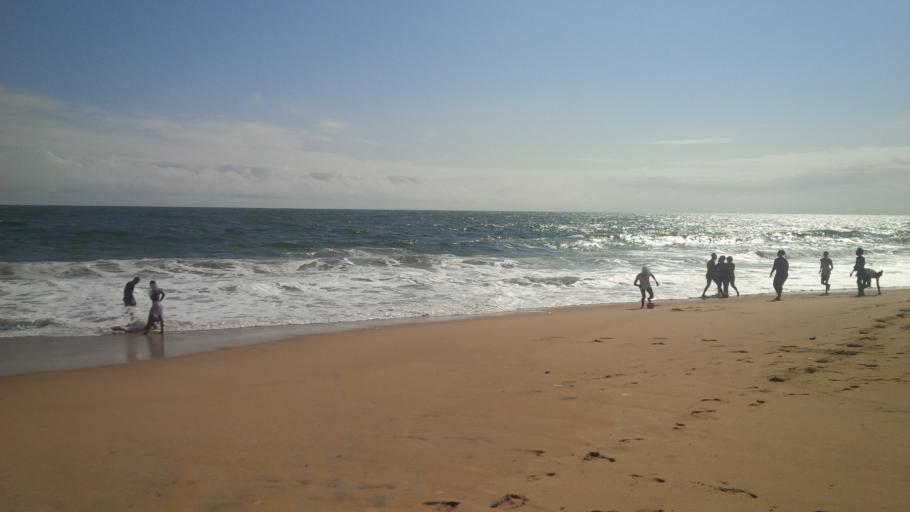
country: CI
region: Sud-Comoe
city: Grand-Bassam
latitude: 5.2218
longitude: -3.8417
